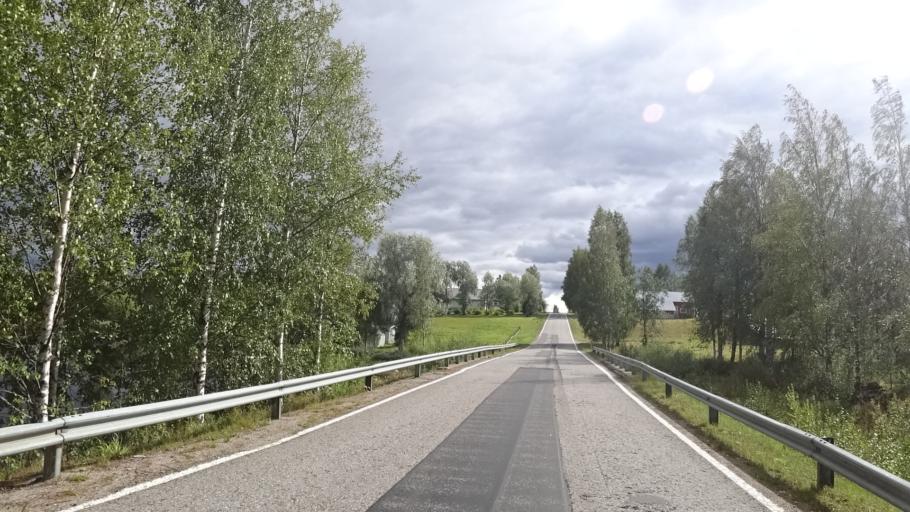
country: FI
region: North Karelia
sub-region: Joensuu
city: Ilomantsi
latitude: 62.4521
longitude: 31.1147
